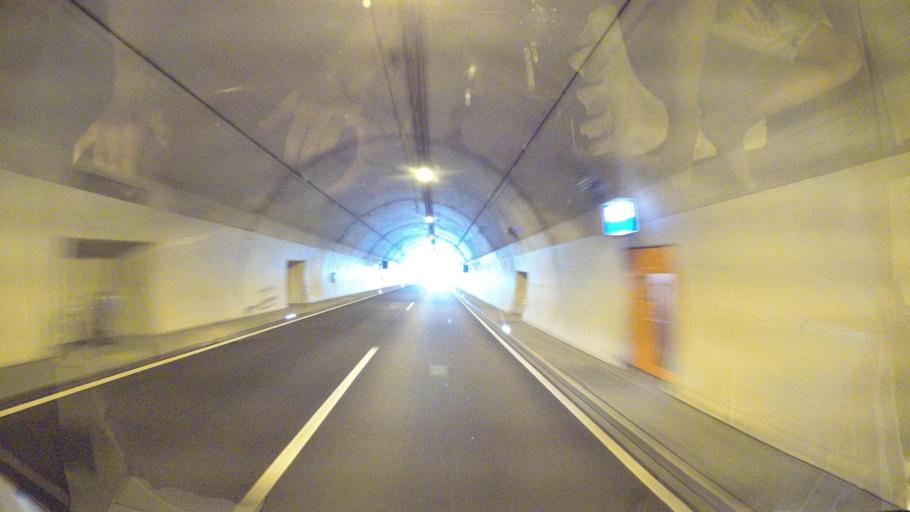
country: DE
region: Baden-Wuerttemberg
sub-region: Freiburg Region
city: Rheinfelden (Baden)
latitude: 47.5725
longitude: 7.7607
